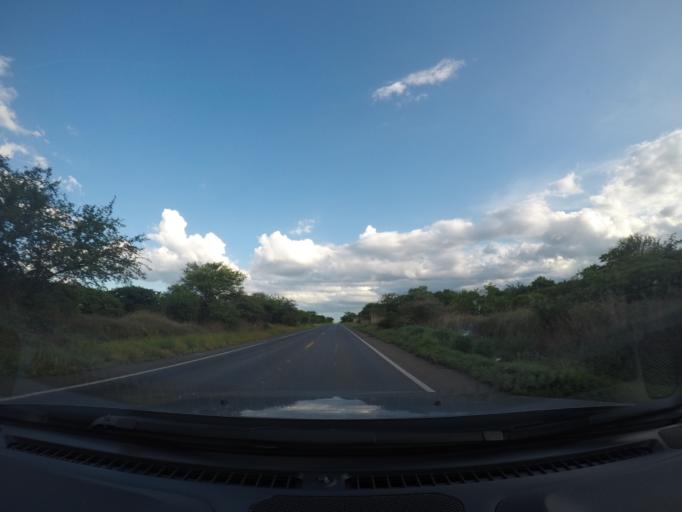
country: BR
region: Bahia
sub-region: Oliveira Dos Brejinhos
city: Beira Rio
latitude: -12.2187
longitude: -42.7939
